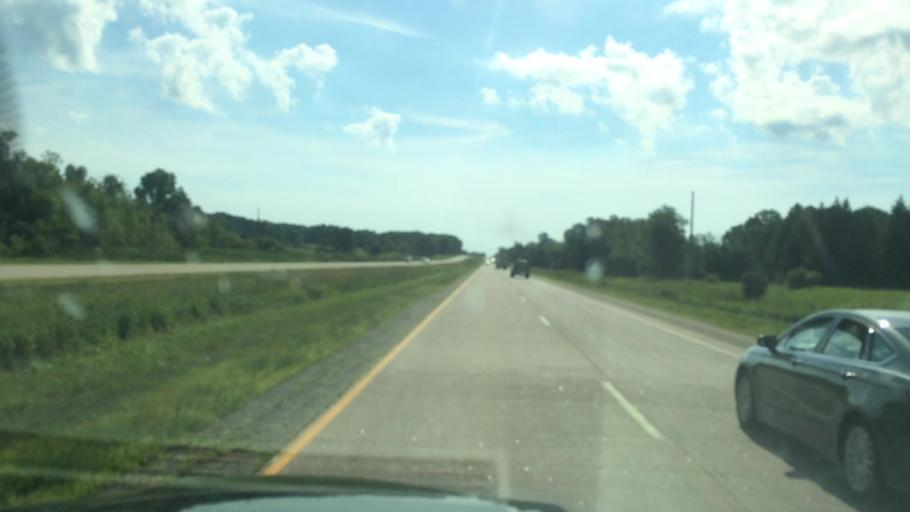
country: US
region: Wisconsin
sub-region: Waupaca County
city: Marion
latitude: 44.8040
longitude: -88.9927
